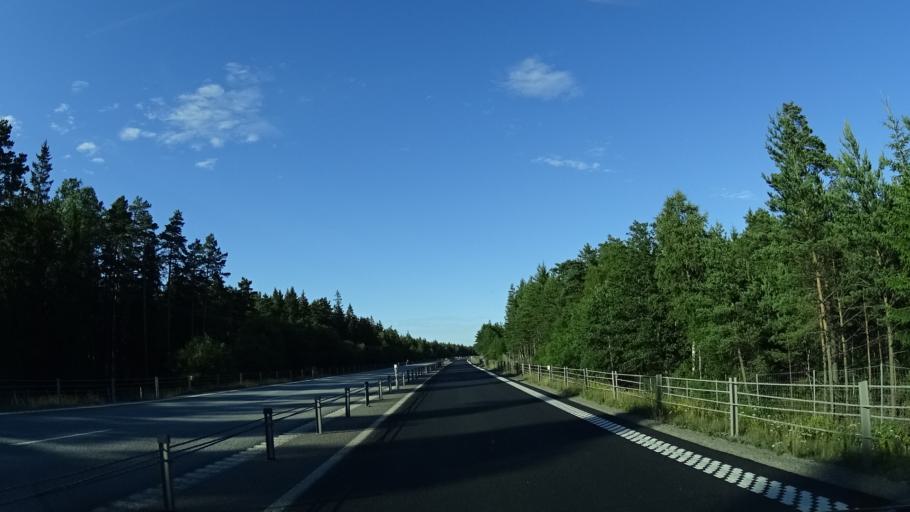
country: SE
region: Stockholm
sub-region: Osterakers Kommun
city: Akersberga
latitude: 59.5837
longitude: 18.2503
